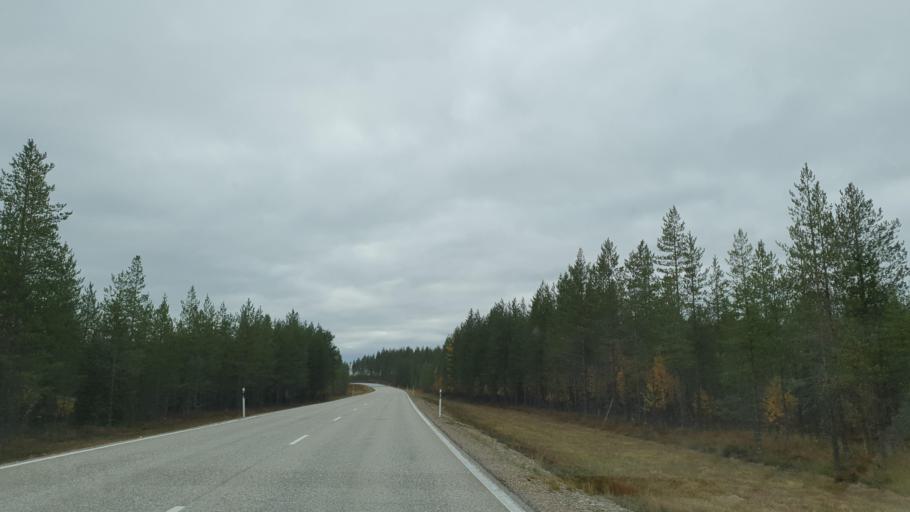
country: FI
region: Northern Ostrobothnia
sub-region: Oulunkaari
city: Pudasjaervi
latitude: 65.5623
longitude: 26.7468
